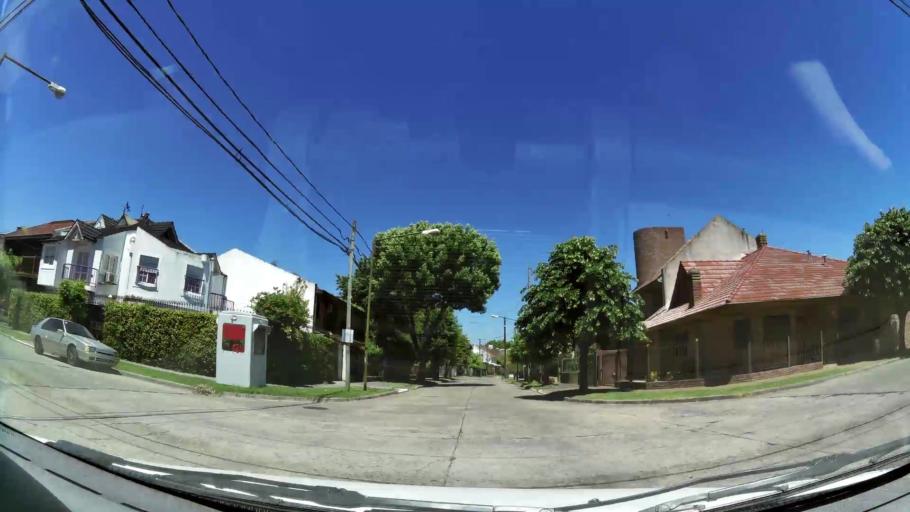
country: AR
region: Buenos Aires
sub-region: Partido de Vicente Lopez
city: Olivos
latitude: -34.5171
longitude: -58.5418
